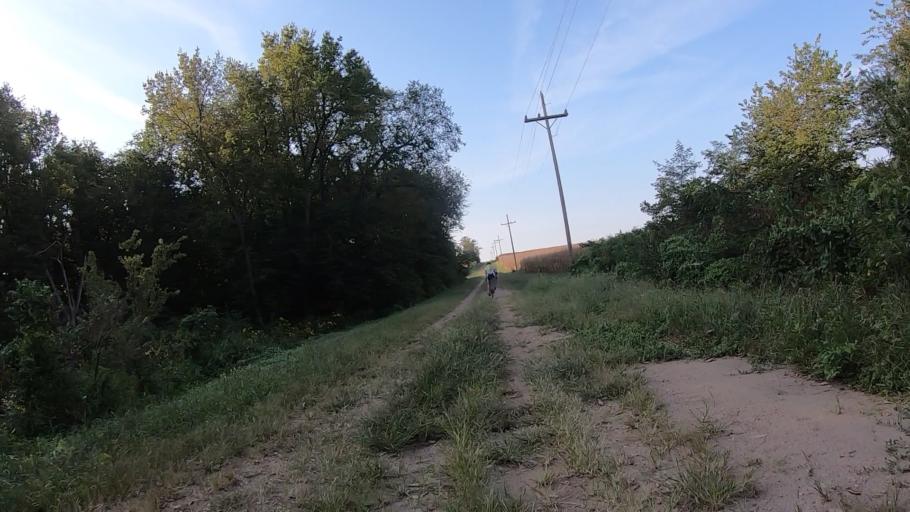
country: US
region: Kansas
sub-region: Marshall County
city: Blue Rapids
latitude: 39.7112
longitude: -96.7792
